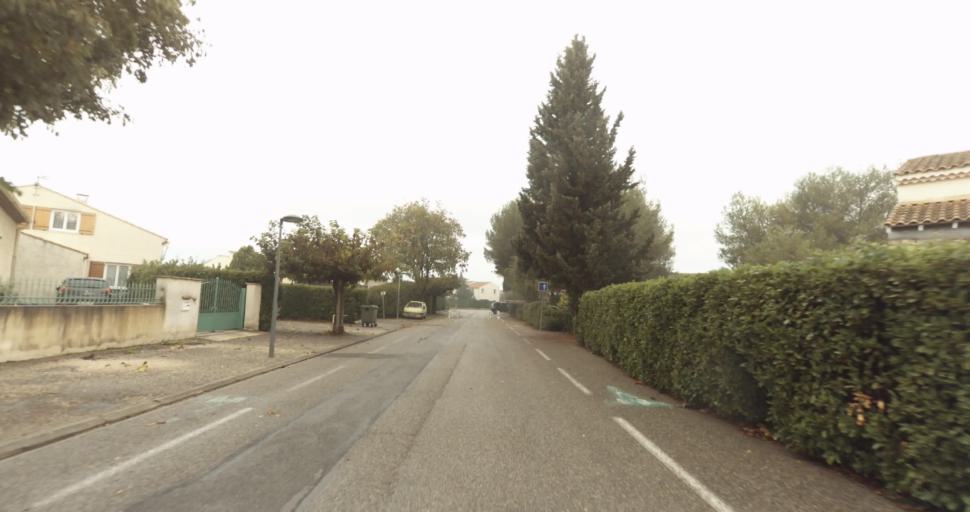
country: FR
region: Provence-Alpes-Cote d'Azur
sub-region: Departement des Bouches-du-Rhone
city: Rognonas
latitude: 43.9010
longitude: 4.8075
